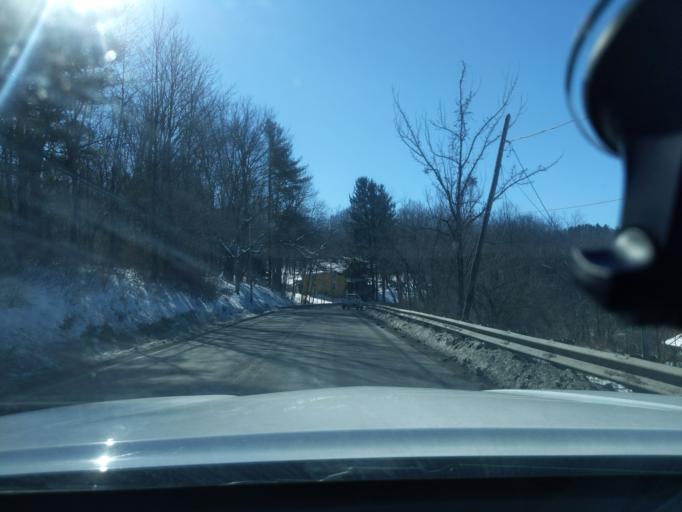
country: US
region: Maryland
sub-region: Allegany County
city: Lonaconing
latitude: 39.6014
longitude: -78.9449
